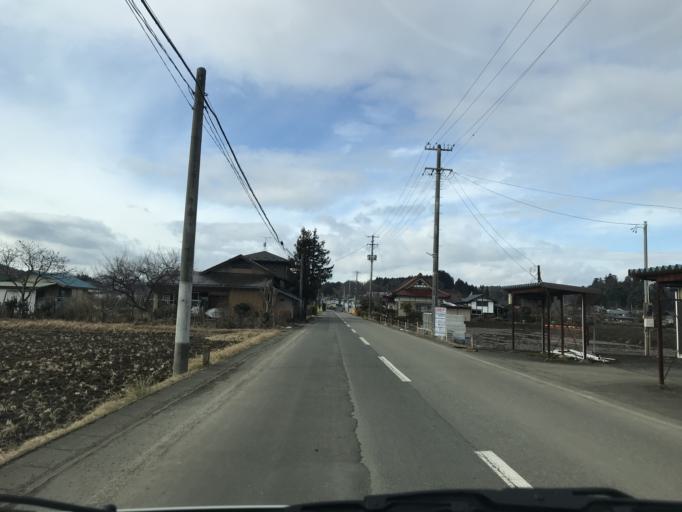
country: JP
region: Iwate
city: Mizusawa
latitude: 39.0944
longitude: 141.1394
